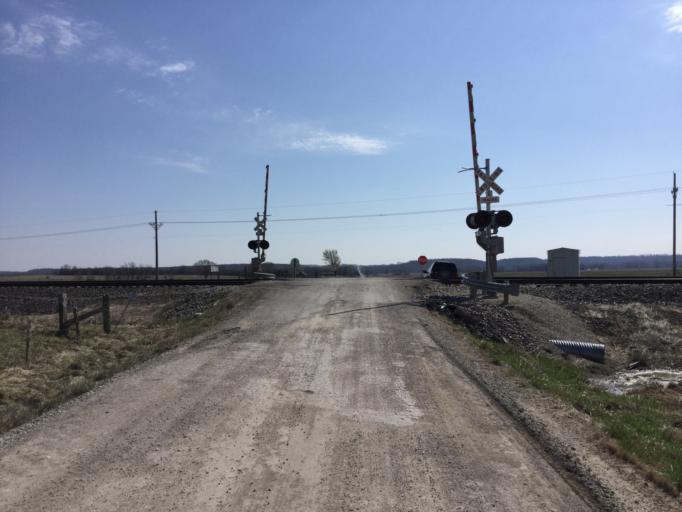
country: US
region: Kansas
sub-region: Anderson County
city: Garnett
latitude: 38.3171
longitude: -95.1901
